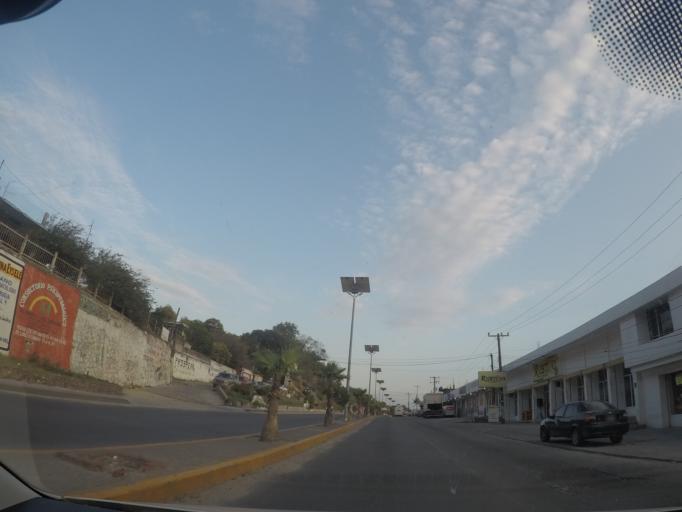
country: MX
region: Oaxaca
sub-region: Salina Cruz
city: Salina Cruz
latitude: 16.1952
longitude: -95.2017
